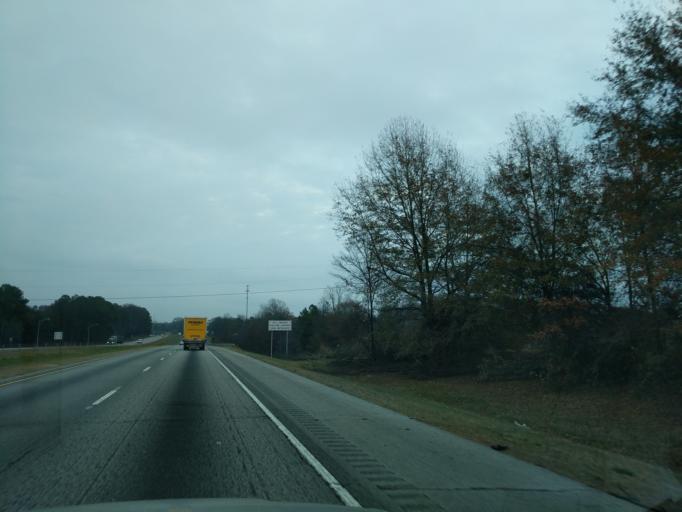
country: US
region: Georgia
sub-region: Franklin County
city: Carnesville
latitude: 34.4141
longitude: -83.1798
